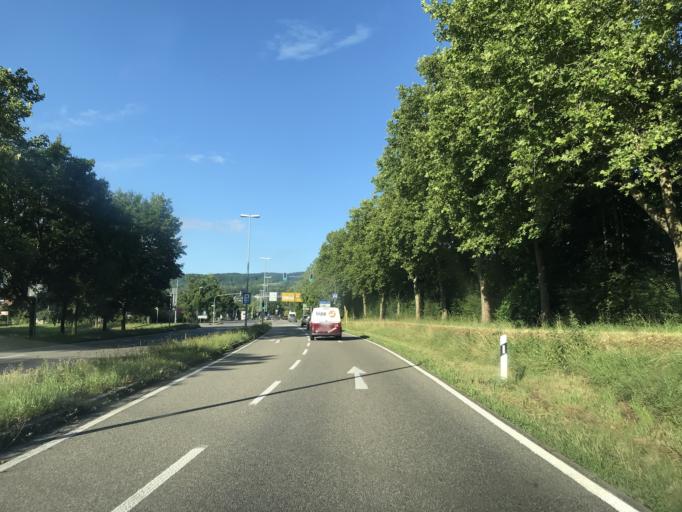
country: DE
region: Baden-Wuerttemberg
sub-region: Freiburg Region
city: Loerrach
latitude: 47.6271
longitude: 7.6610
